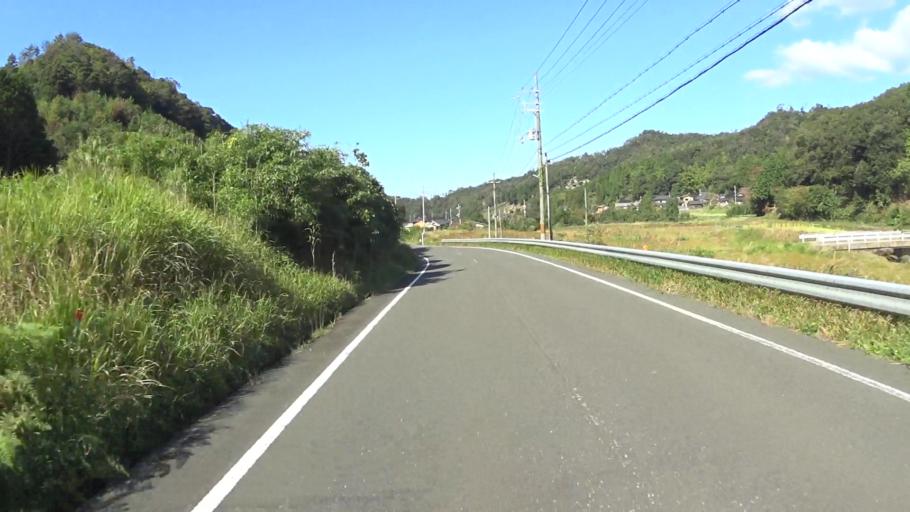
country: JP
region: Hyogo
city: Toyooka
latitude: 35.5595
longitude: 134.9793
